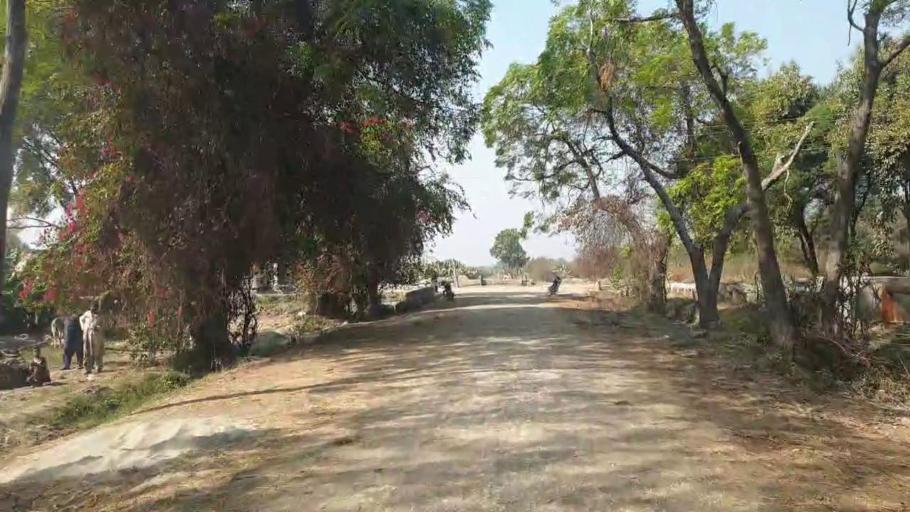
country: PK
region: Sindh
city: Tando Jam
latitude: 25.3439
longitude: 68.6284
